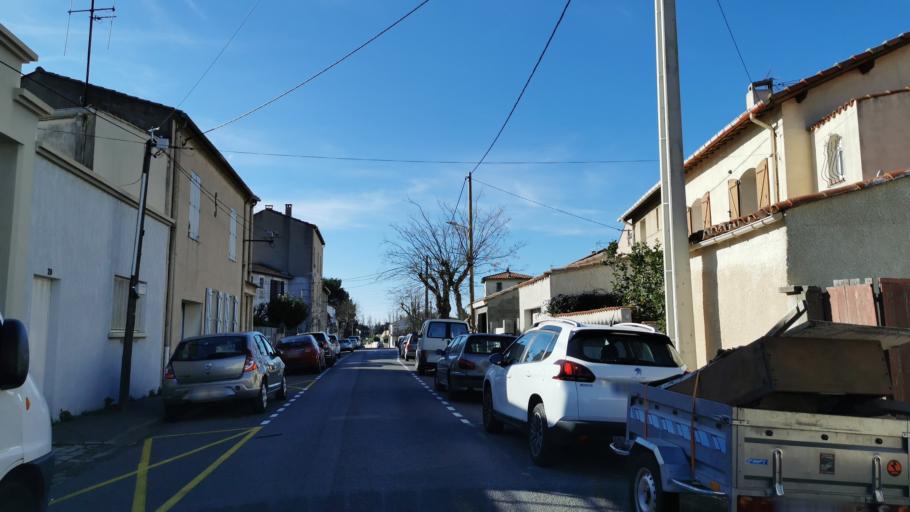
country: FR
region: Languedoc-Roussillon
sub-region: Departement de l'Aude
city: Narbonne
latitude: 43.1784
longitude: 2.9966
